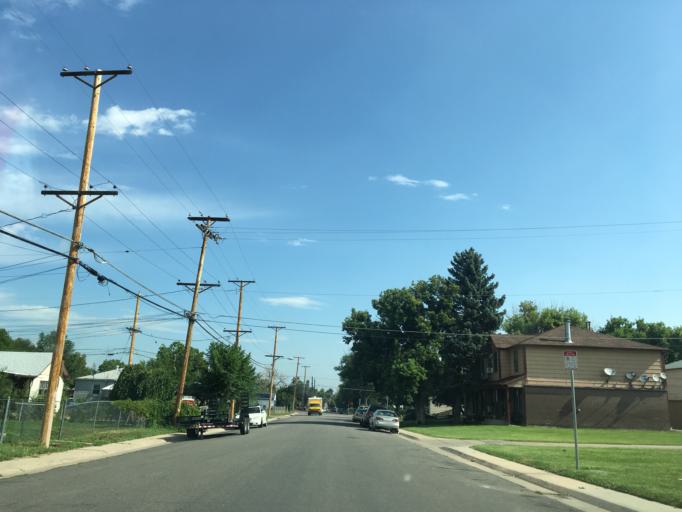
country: US
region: Colorado
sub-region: Jefferson County
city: Lakewood
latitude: 39.7024
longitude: -105.0391
